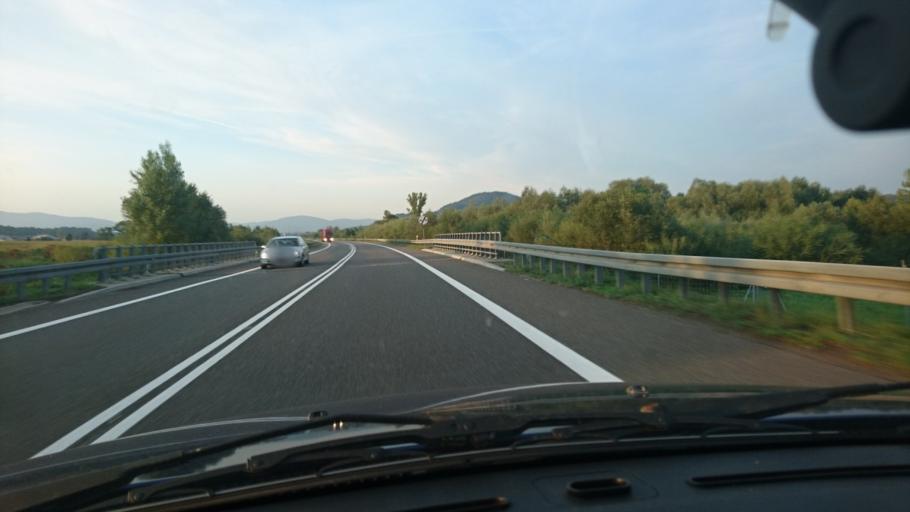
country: PL
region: Silesian Voivodeship
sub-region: Powiat zywiecki
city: Wieprz
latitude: 49.6373
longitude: 19.1654
